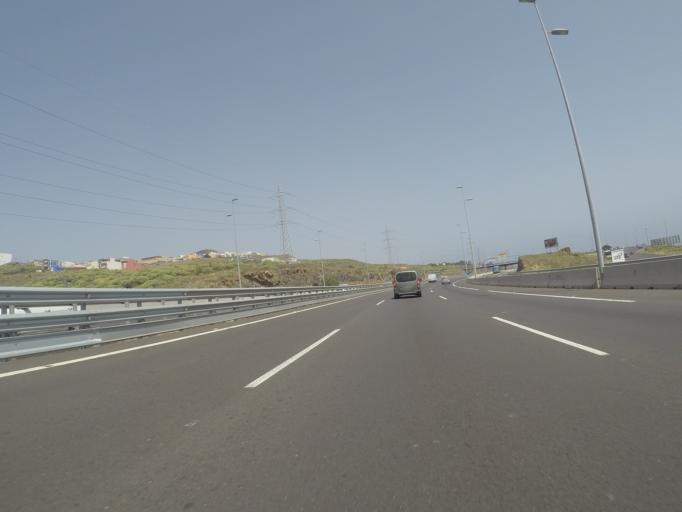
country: ES
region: Canary Islands
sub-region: Provincia de Santa Cruz de Tenerife
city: La Laguna
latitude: 28.4303
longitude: -16.3011
